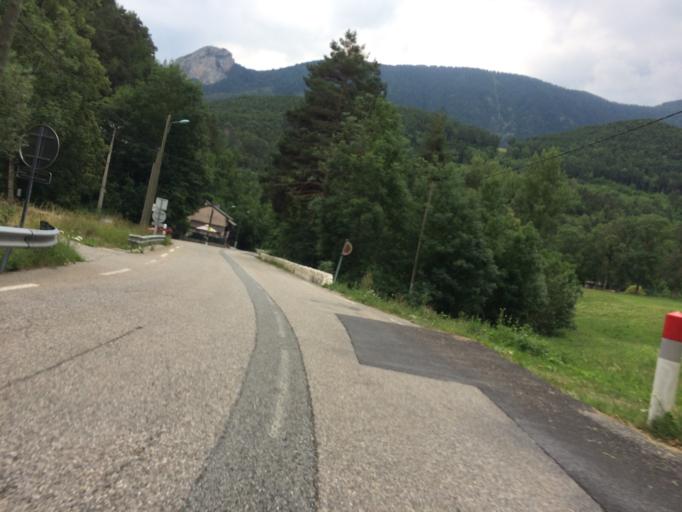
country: FR
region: Provence-Alpes-Cote d'Azur
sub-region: Departement des Alpes-Maritimes
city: Tende
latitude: 44.1127
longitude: 7.5655
